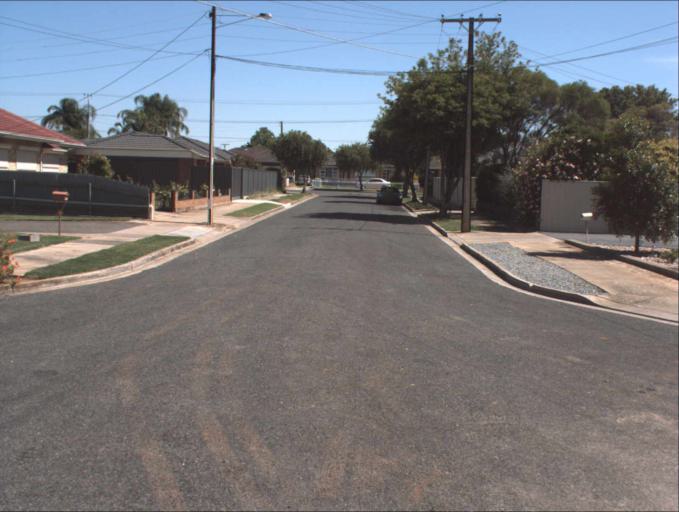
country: AU
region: South Australia
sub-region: Port Adelaide Enfield
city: Klemzig
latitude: -34.8847
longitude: 138.6394
